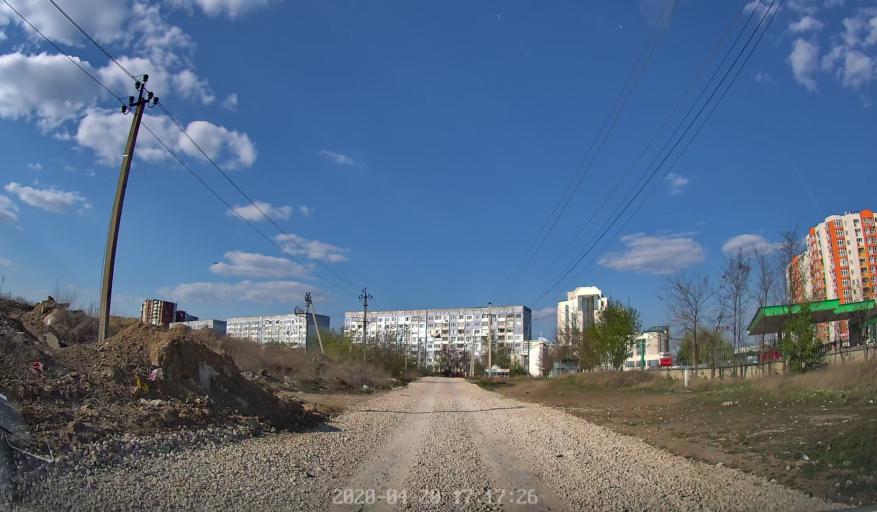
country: MD
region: Chisinau
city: Chisinau
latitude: 46.9734
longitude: 28.8470
